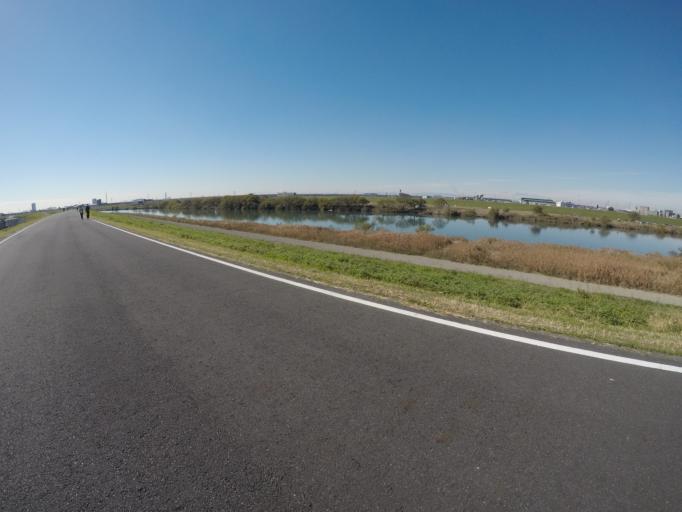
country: JP
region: Chiba
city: Matsudo
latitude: 35.8115
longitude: 139.8921
